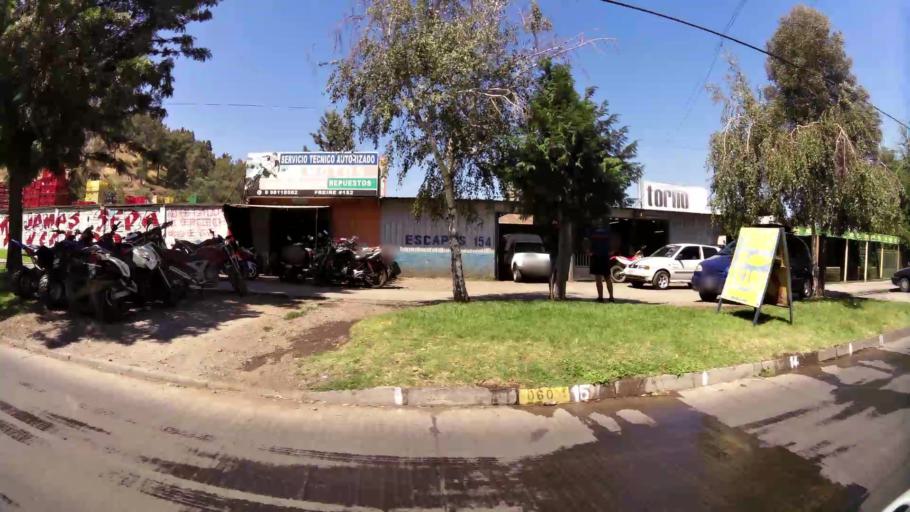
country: CL
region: Maule
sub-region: Provincia de Curico
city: Curico
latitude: -34.9772
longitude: -71.2332
